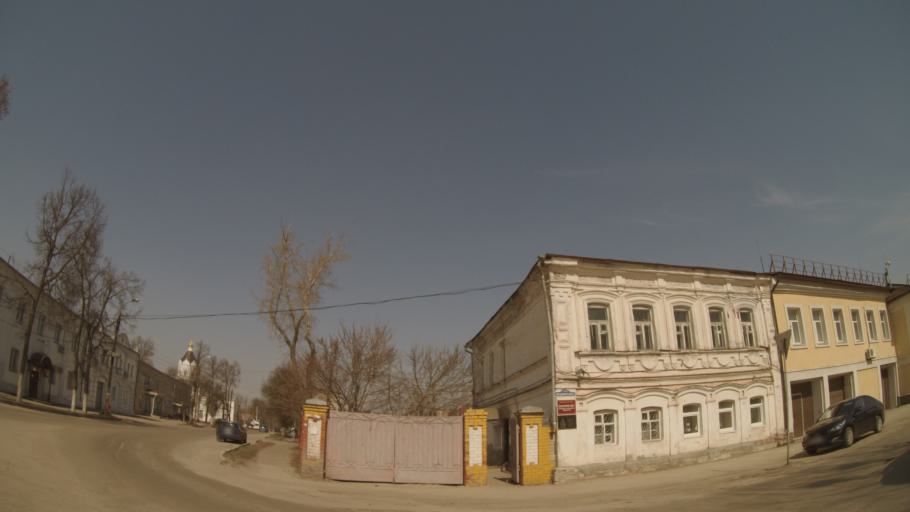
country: RU
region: Nizjnij Novgorod
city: Arzamas
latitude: 55.3882
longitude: 43.8133
